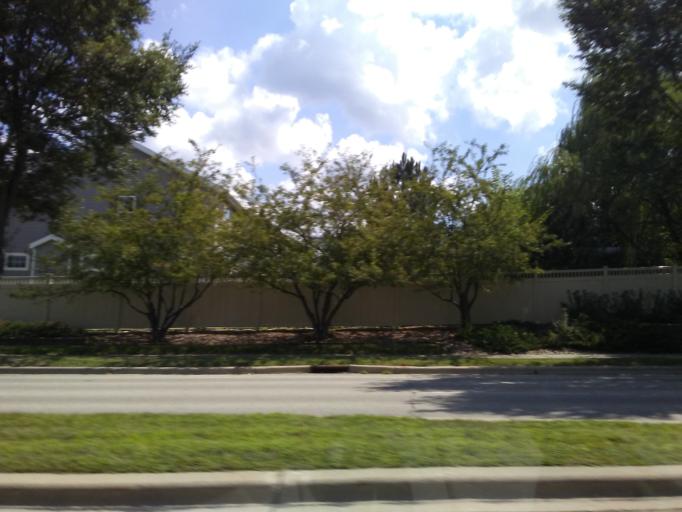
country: US
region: Wisconsin
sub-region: Dane County
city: Verona
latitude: 43.0380
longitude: -89.5183
